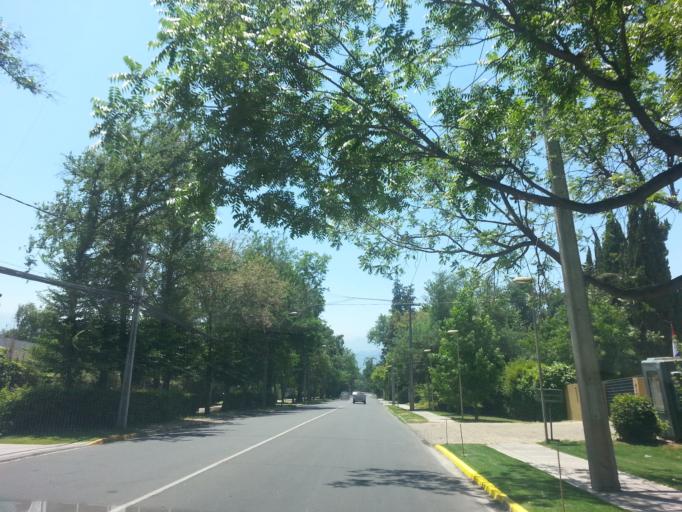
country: CL
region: Santiago Metropolitan
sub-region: Provincia de Santiago
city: Villa Presidente Frei, Nunoa, Santiago, Chile
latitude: -33.3824
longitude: -70.5241
